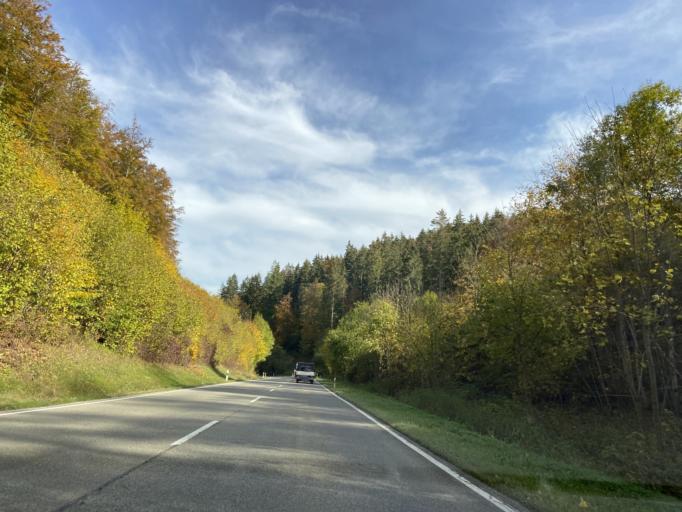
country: DE
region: Baden-Wuerttemberg
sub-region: Tuebingen Region
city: Stetten am Kalten Markt
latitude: 48.1279
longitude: 9.0994
